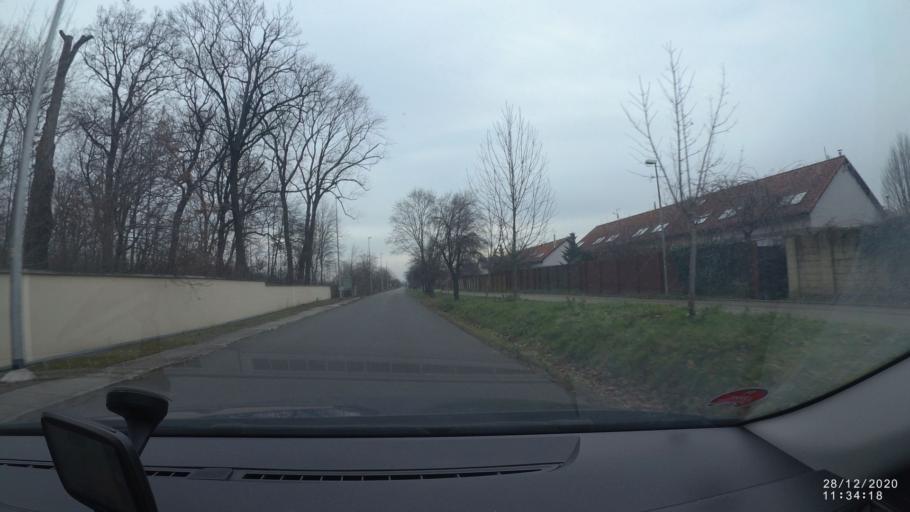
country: CZ
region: Praha
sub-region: Praha 19
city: Satalice
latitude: 50.1272
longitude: 14.5795
